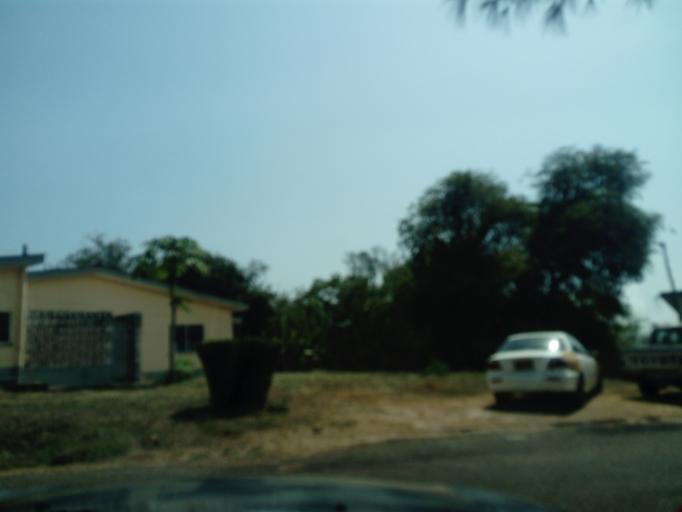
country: GH
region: Central
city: Cape Coast
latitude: 5.1104
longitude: -1.2842
